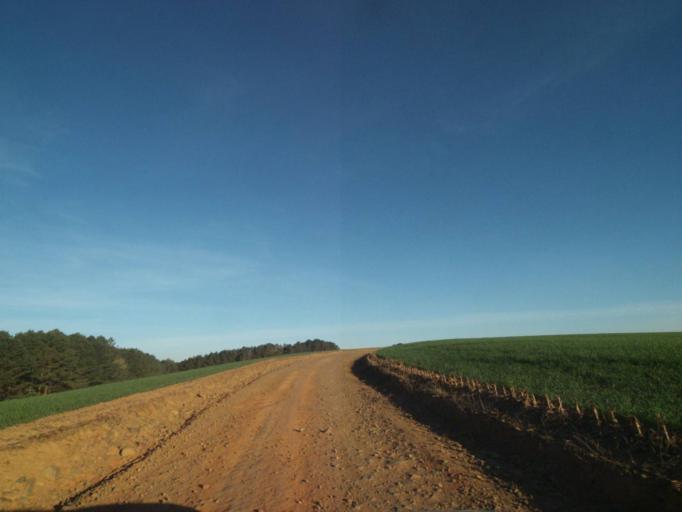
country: BR
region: Parana
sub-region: Telemaco Borba
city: Telemaco Borba
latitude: -24.4650
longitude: -50.5964
